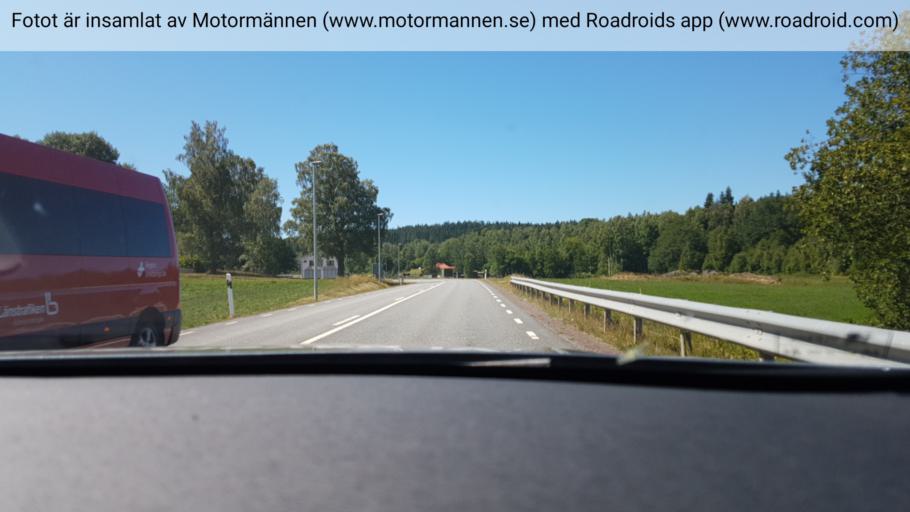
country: SE
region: Joenkoeping
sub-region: Jonkopings Kommun
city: Asa
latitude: 58.0099
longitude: 14.5629
